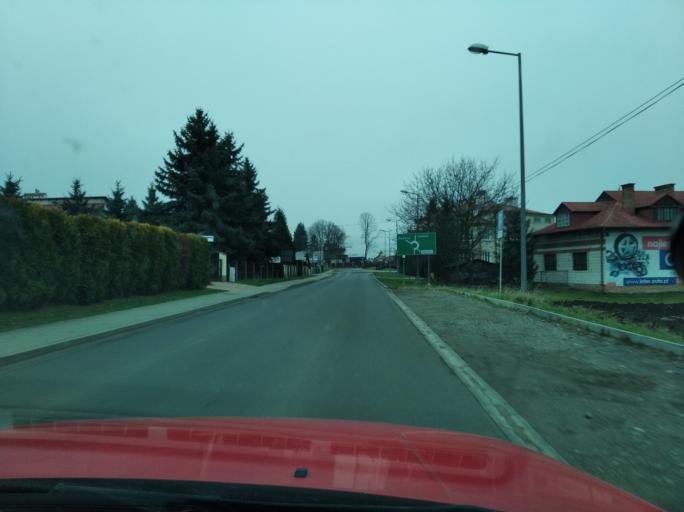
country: PL
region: Subcarpathian Voivodeship
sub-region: Powiat jaroslawski
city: Pawlosiow
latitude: 50.0139
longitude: 22.6454
